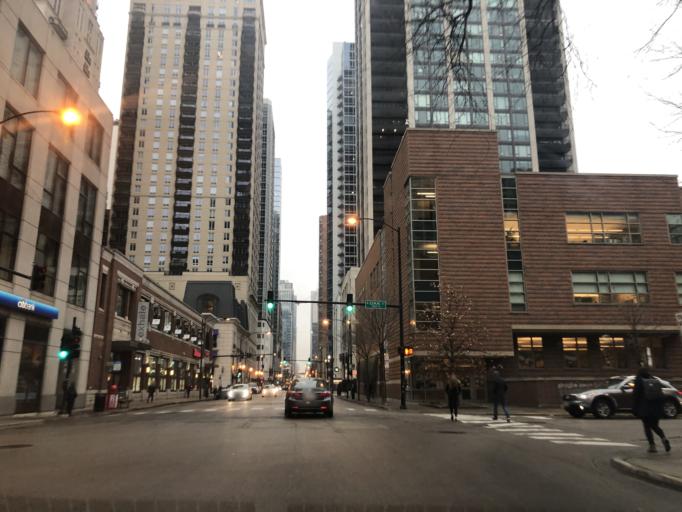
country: US
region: Illinois
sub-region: Cook County
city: Chicago
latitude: 41.9008
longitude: -87.6283
